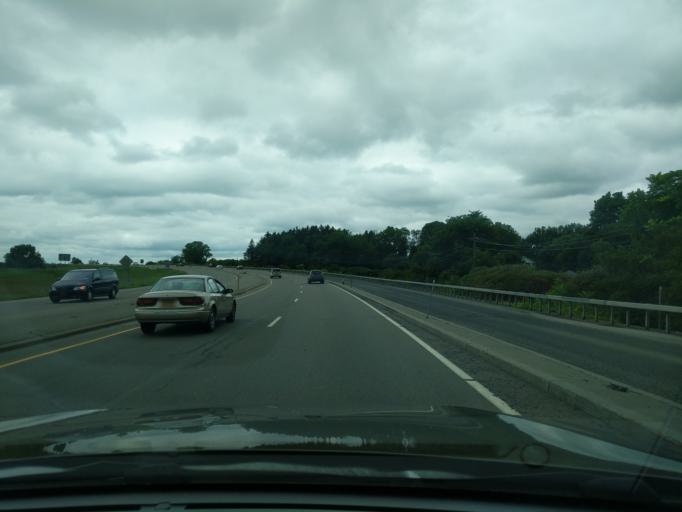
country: US
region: New York
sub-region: Chemung County
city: Horseheads
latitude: 42.1635
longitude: -76.8414
